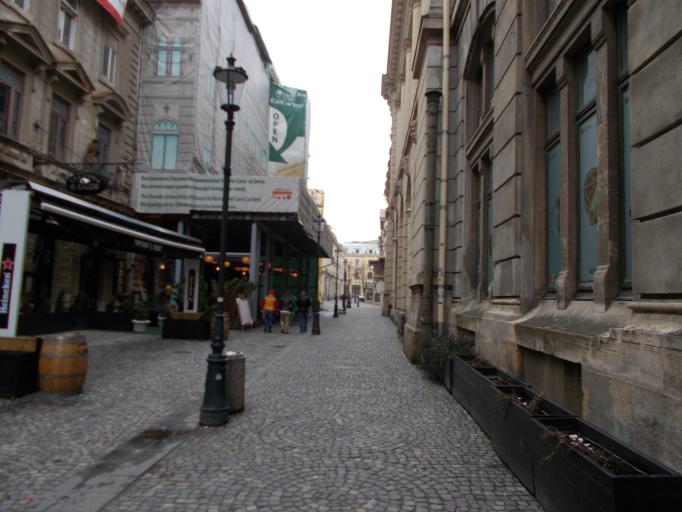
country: RO
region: Bucuresti
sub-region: Municipiul Bucuresti
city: Bucuresti
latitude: 44.4319
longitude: 26.0980
